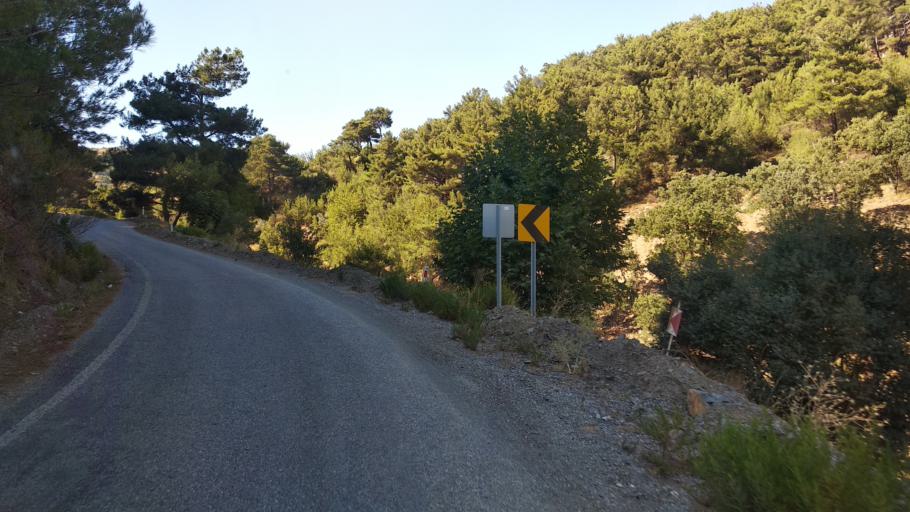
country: TR
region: Izmir
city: Gaziemir
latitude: 38.3261
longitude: 26.9568
